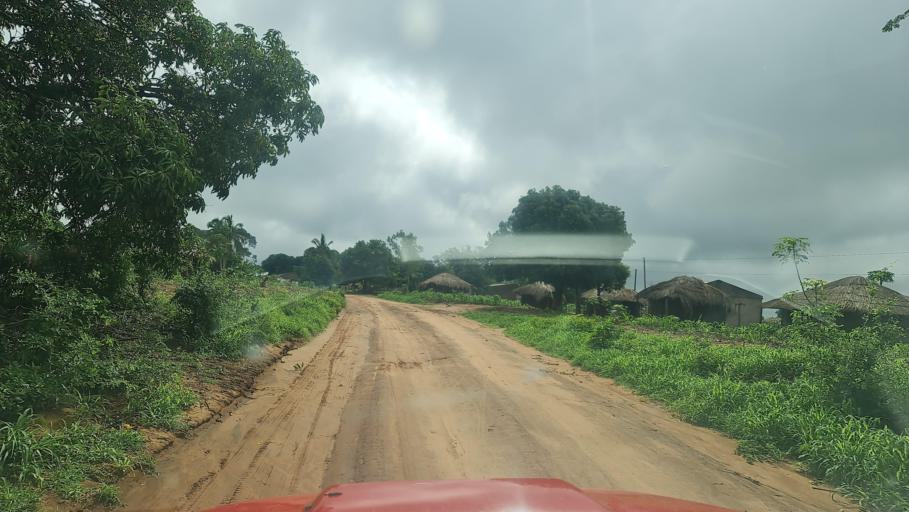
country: MW
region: Southern Region
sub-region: Nsanje District
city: Nsanje
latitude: -17.2033
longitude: 35.6953
